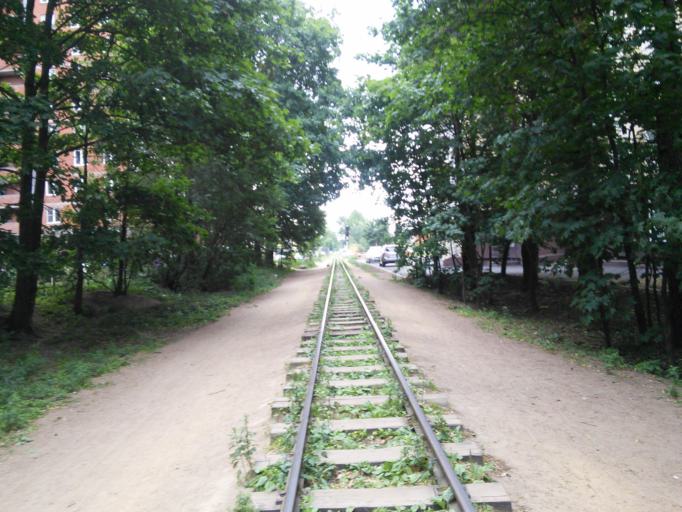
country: RU
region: St.-Petersburg
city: Kolomyagi
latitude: 60.0289
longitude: 30.2934
